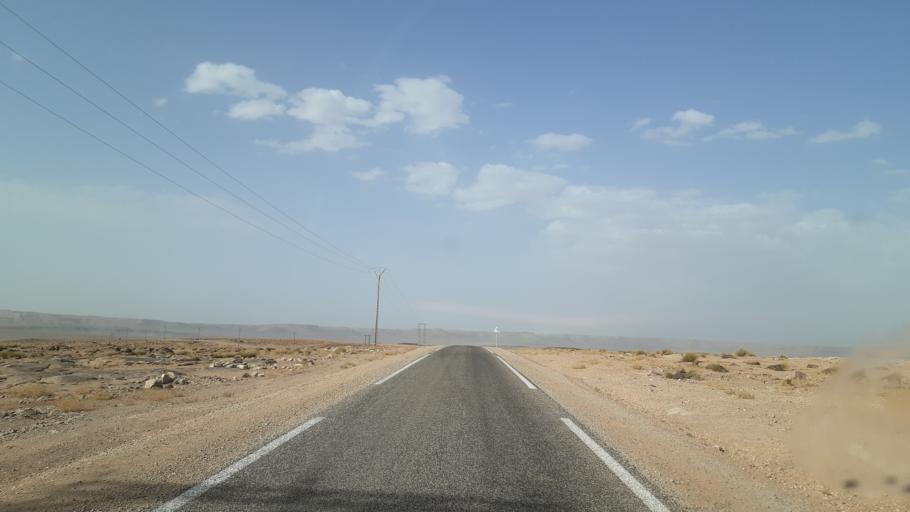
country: MA
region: Meknes-Tafilalet
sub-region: Khenifra
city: Midelt
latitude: 32.8602
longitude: -4.6960
